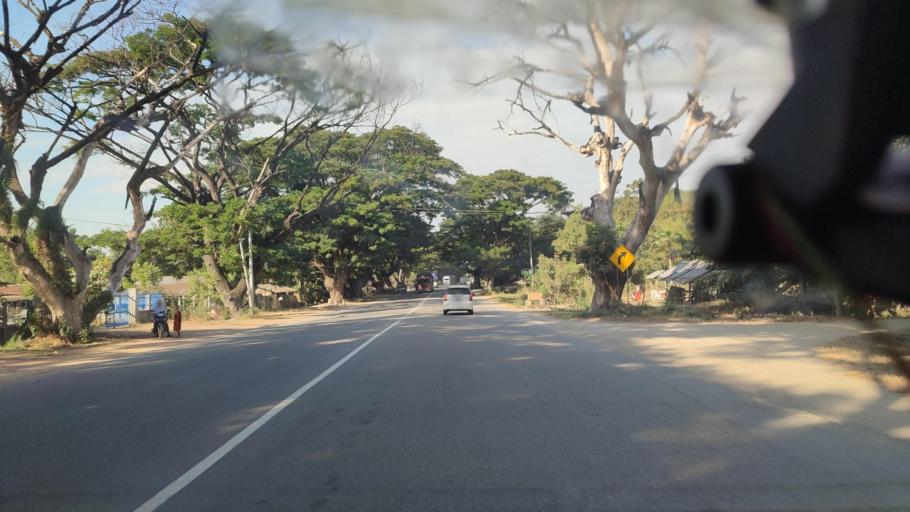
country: MM
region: Mandalay
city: Pyinmana
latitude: 20.0447
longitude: 96.2484
